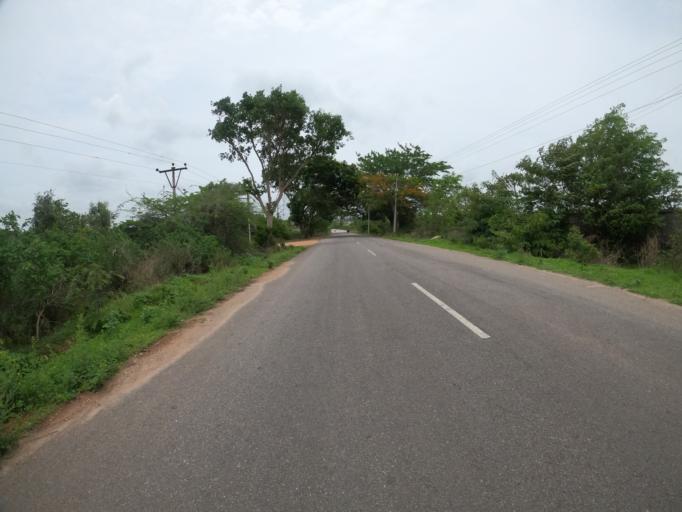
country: IN
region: Telangana
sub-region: Hyderabad
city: Hyderabad
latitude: 17.3450
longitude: 78.3606
